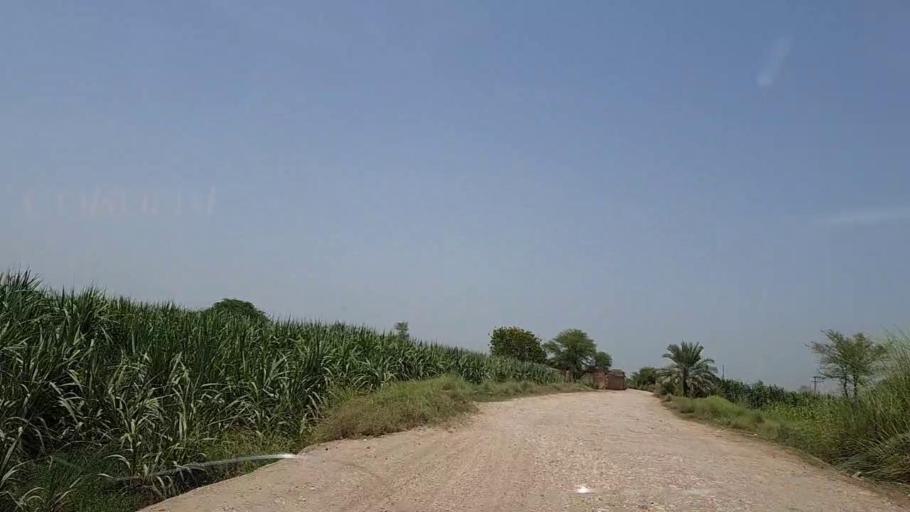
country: PK
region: Sindh
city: Tharu Shah
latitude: 26.9240
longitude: 68.0560
